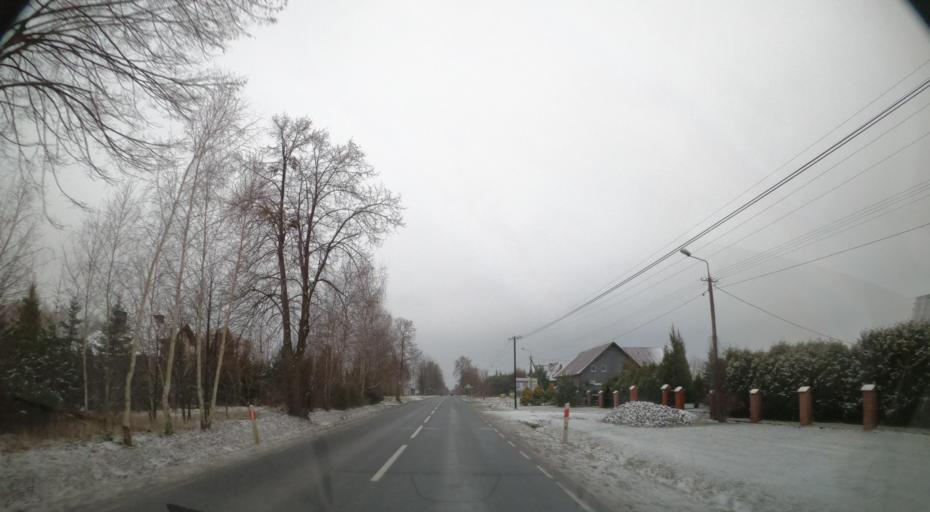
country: PL
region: Masovian Voivodeship
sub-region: Powiat plocki
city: Maszewo Duze
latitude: 52.5710
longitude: 19.6080
